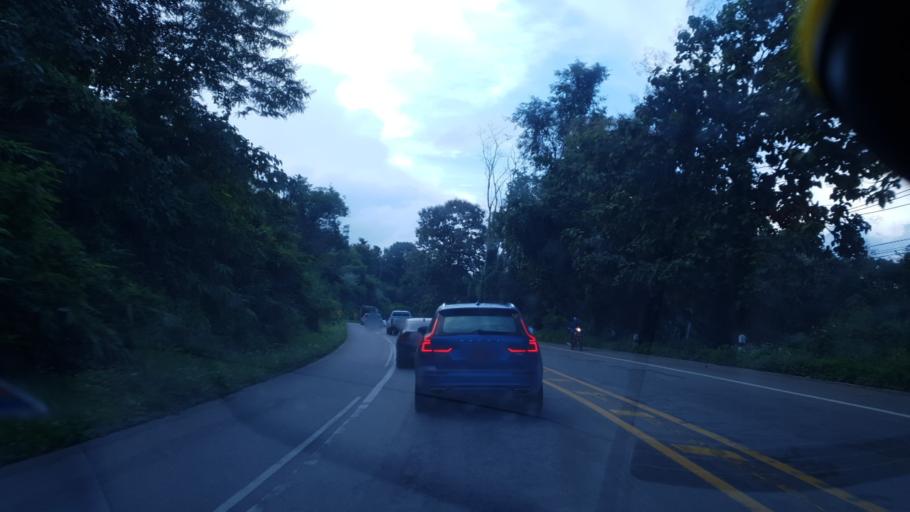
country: TH
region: Chiang Rai
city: Mae Suai
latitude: 19.6803
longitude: 99.5669
